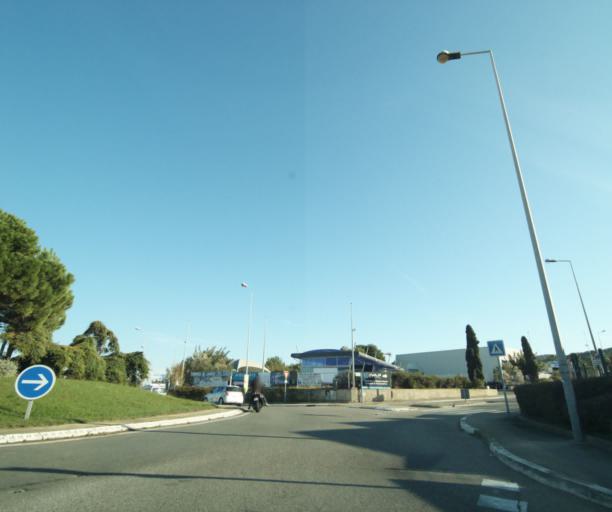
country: FR
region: Provence-Alpes-Cote d'Azur
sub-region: Departement des Bouches-du-Rhone
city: Chateauneuf-les-Martigues
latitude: 43.3943
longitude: 5.1366
